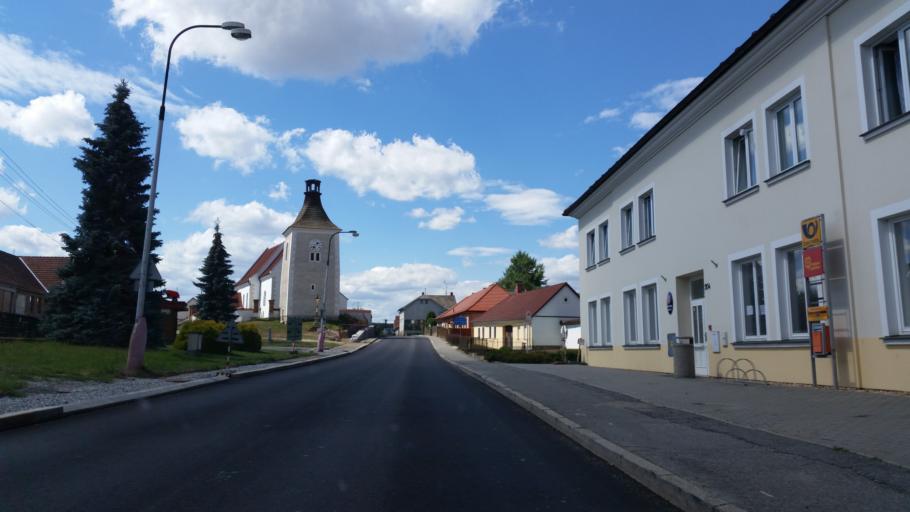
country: CZ
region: Vysocina
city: Cernovice
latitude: 49.4248
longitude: 14.9458
